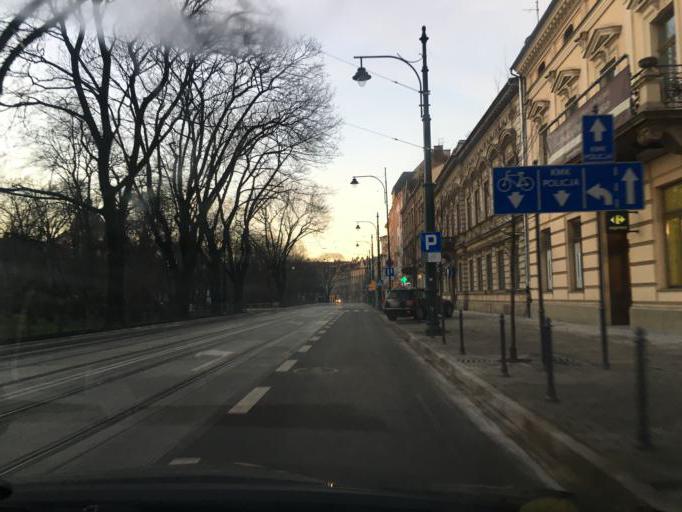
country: PL
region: Lesser Poland Voivodeship
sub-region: Krakow
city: Krakow
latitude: 50.0646
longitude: 19.9342
